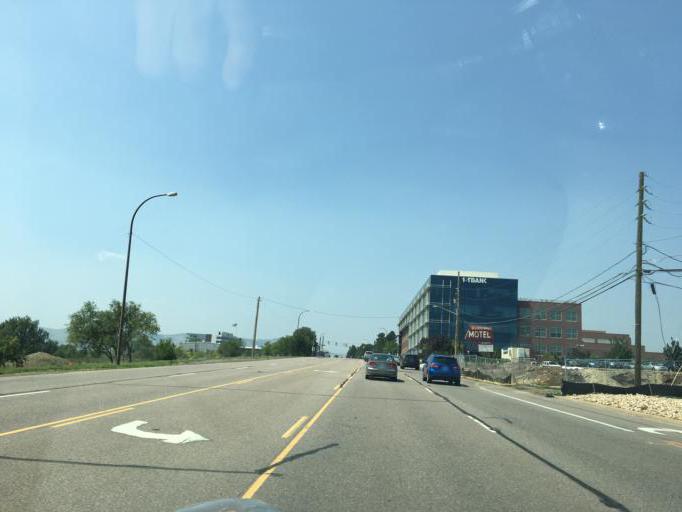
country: US
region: Colorado
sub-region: Jefferson County
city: Applewood
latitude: 39.7402
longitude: -105.1336
